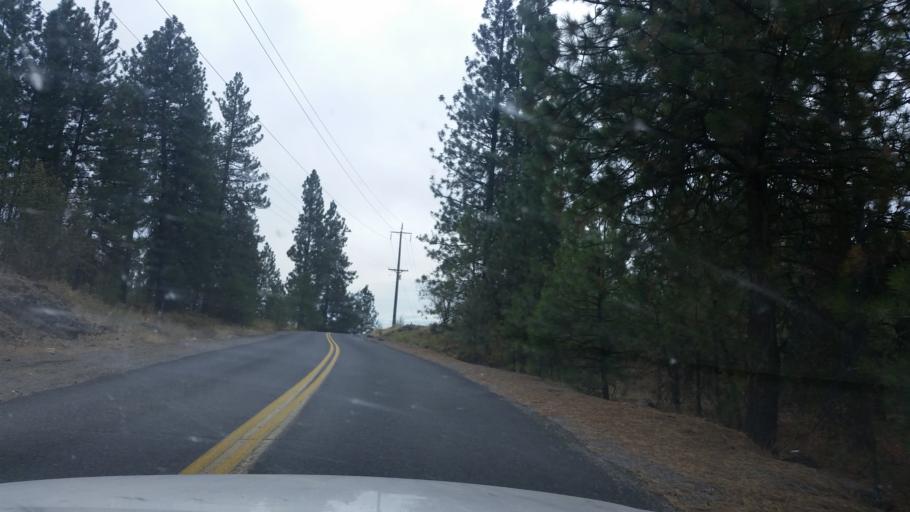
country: US
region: Washington
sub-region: Spokane County
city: Spokane
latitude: 47.6464
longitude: -117.4970
